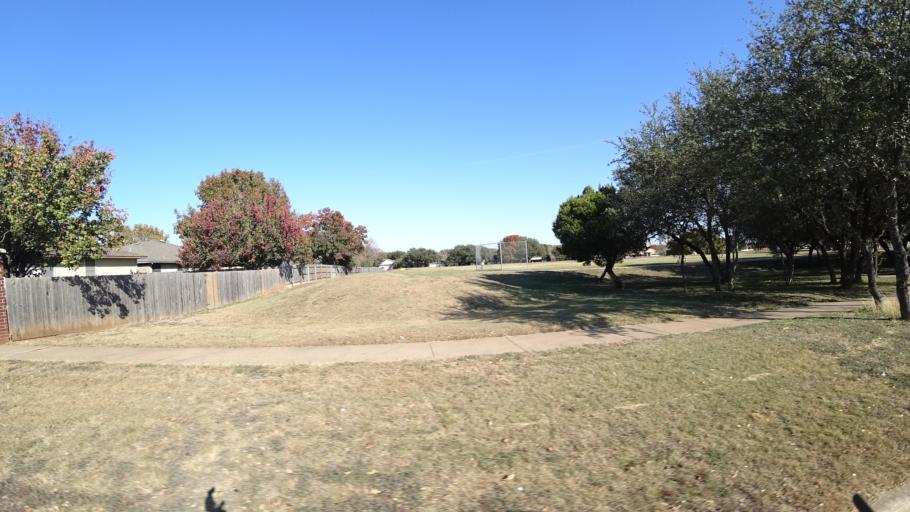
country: US
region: Texas
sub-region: Williamson County
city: Cedar Park
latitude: 30.5172
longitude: -97.8522
